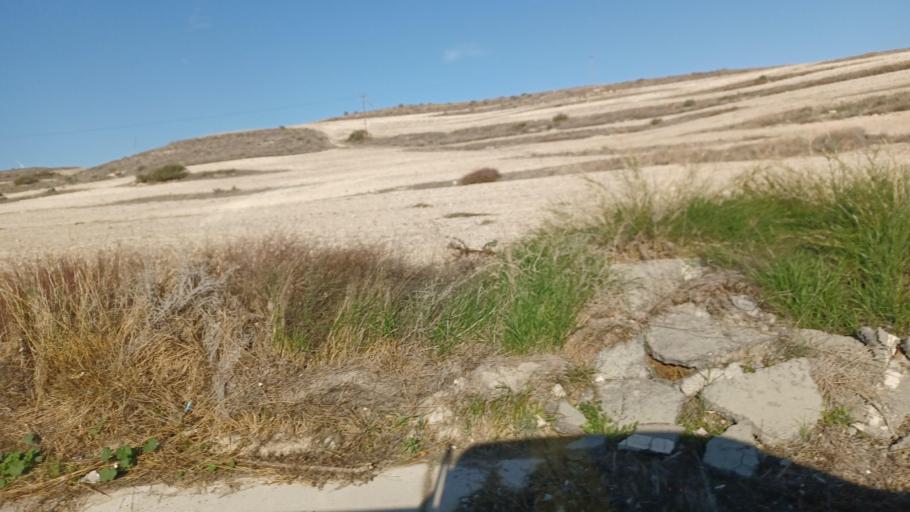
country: CY
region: Larnaka
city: Psevdas
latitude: 34.9688
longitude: 33.5159
